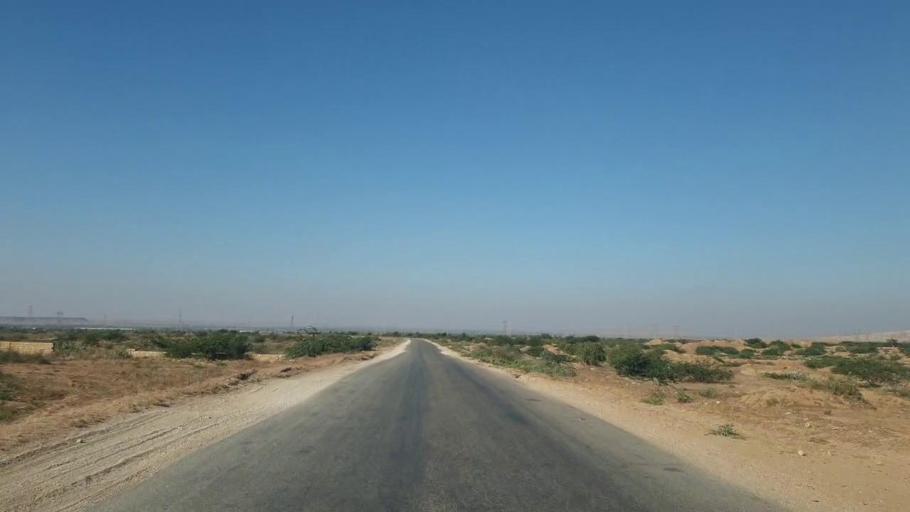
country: PK
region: Sindh
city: Gharo
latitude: 25.1638
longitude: 67.6626
